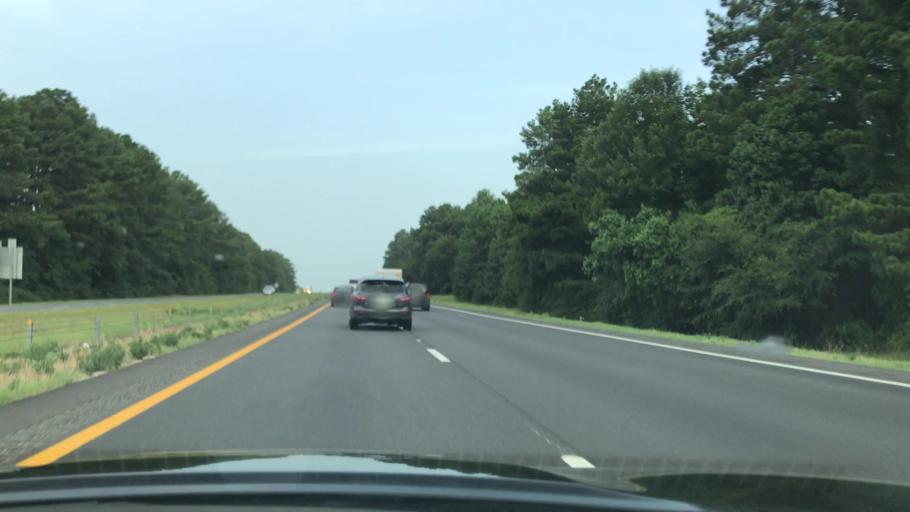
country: US
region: Texas
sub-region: Gregg County
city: Longview
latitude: 32.4594
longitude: -94.6723
